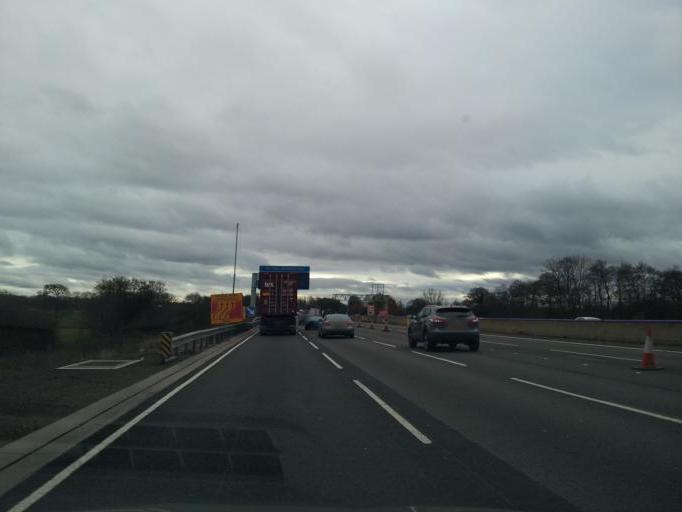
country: GB
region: England
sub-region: Staffordshire
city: Penkridge
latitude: 52.7016
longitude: -2.1030
